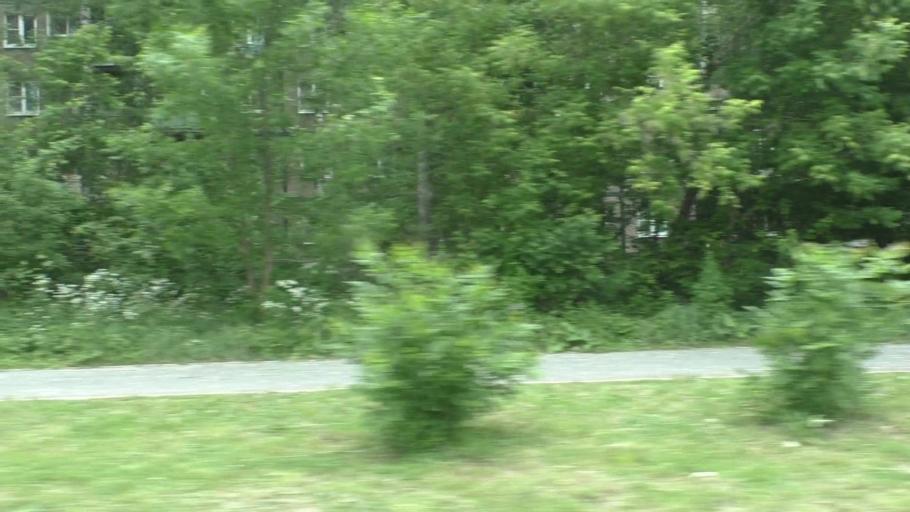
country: RU
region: Moskovskaya
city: Yegor'yevsk
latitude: 55.3693
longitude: 39.0531
